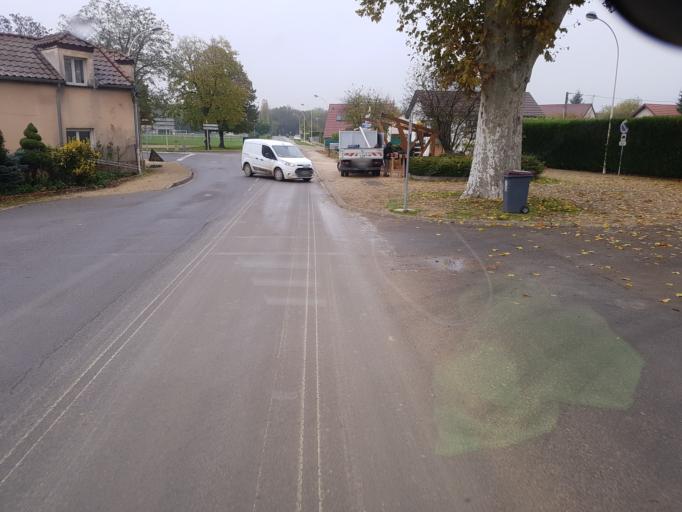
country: FR
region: Bourgogne
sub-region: Departement de la Cote-d'Or
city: Arc-sur-Tille
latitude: 47.3173
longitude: 5.2068
